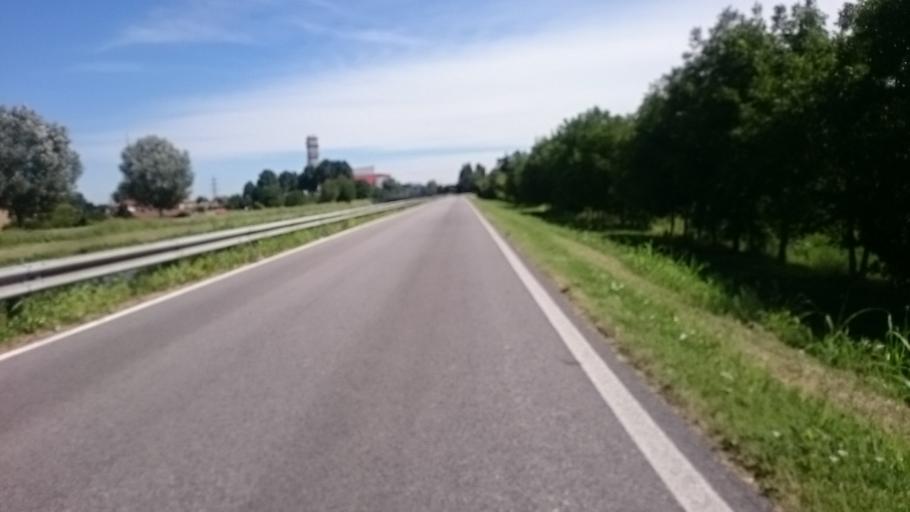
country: IT
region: Veneto
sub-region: Provincia di Padova
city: Padova
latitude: 45.4014
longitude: 11.9185
